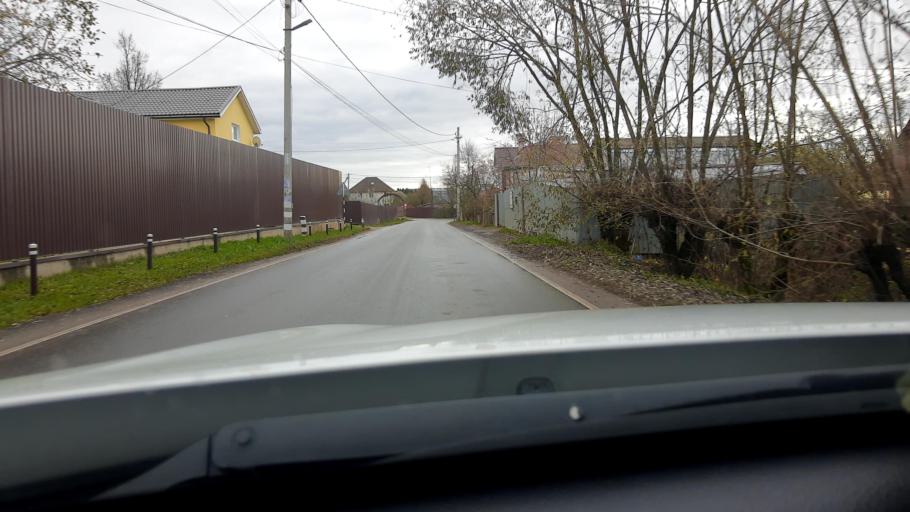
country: RU
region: Moskovskaya
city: Annino
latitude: 55.5663
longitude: 37.2356
